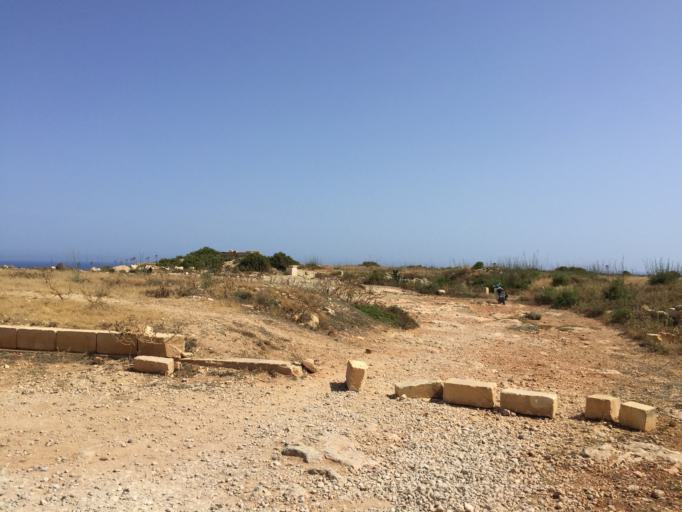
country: MT
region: In-Nadur
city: Nadur
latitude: 36.0631
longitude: 14.2896
